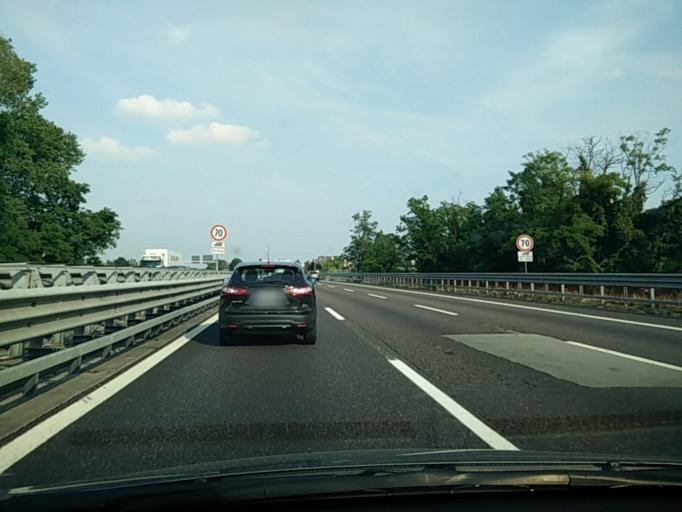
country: IT
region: Lombardy
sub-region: Citta metropolitana di Milano
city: Trezzano sul Naviglio
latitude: 45.4168
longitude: 9.0863
